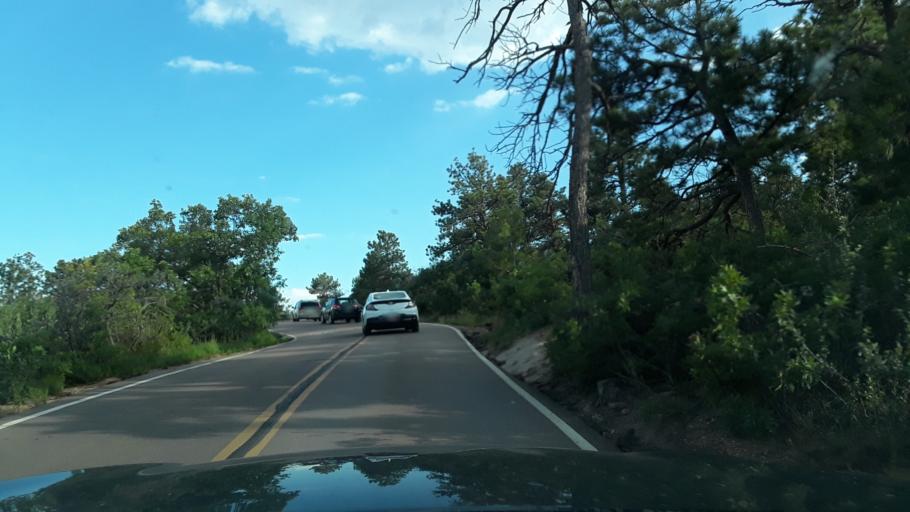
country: US
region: Colorado
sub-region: El Paso County
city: Colorado Springs
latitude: 38.8782
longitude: -104.7683
